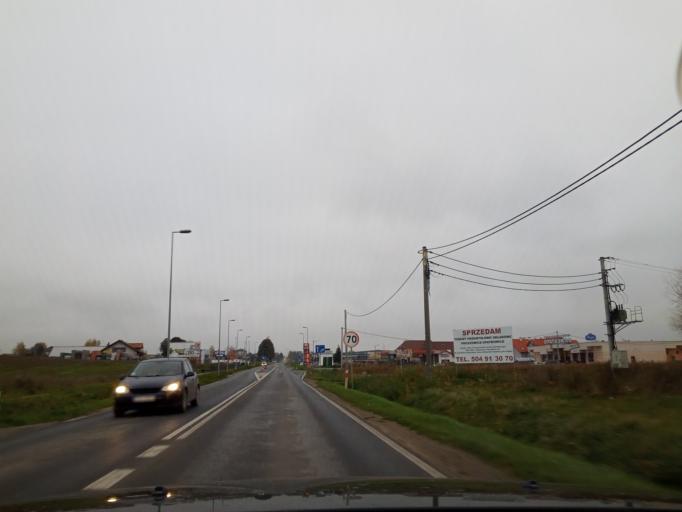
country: PL
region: Lesser Poland Voivodeship
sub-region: Powiat proszowicki
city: Proszowice
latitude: 50.2002
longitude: 20.3013
